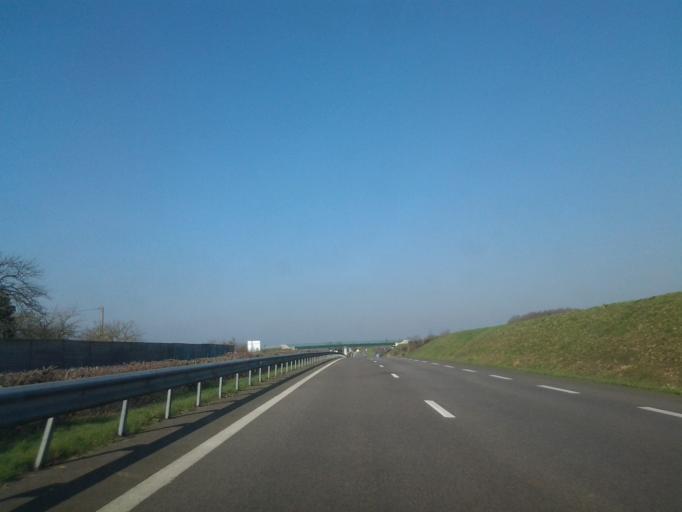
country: FR
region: Pays de la Loire
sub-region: Departement de la Vendee
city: Saint-Christophe-du-Ligneron
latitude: 46.8084
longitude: -1.7412
